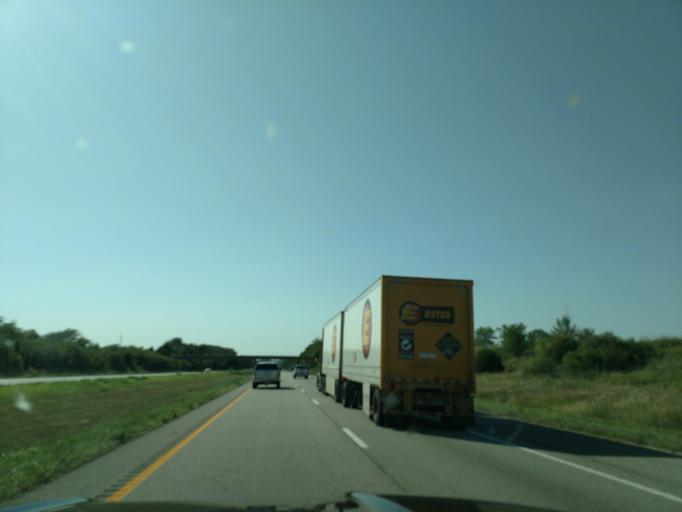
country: US
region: Missouri
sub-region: Andrew County
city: Savannah
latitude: 39.8920
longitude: -94.8656
